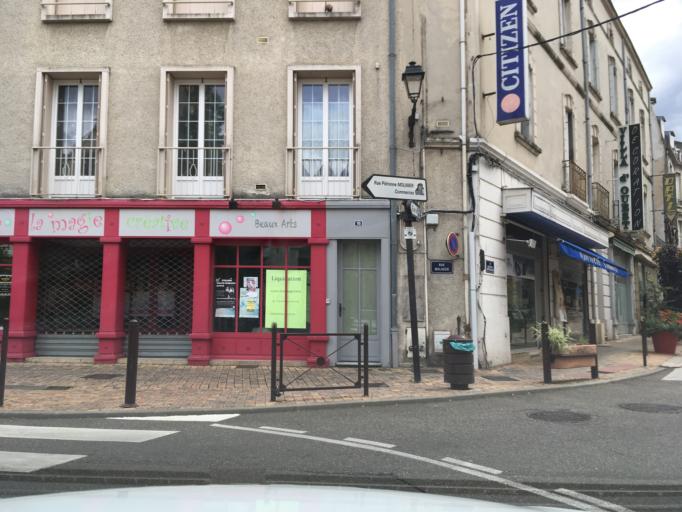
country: FR
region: Aquitaine
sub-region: Departement du Lot-et-Garonne
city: Agen
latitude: 44.2060
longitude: 0.6190
